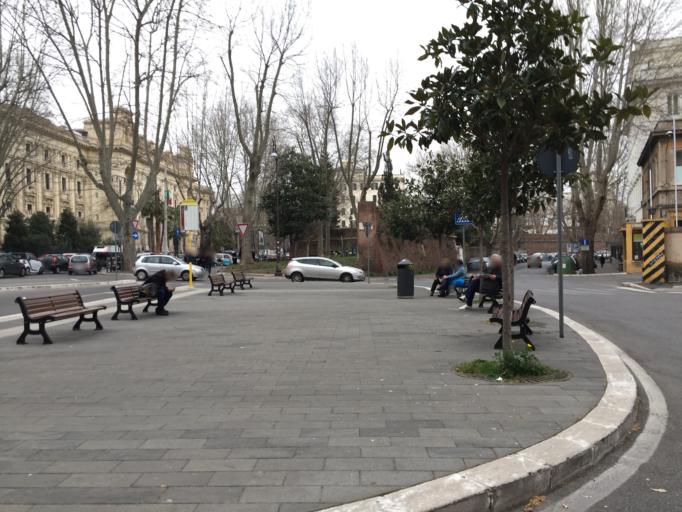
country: VA
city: Vatican City
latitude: 41.8835
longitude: 12.4697
